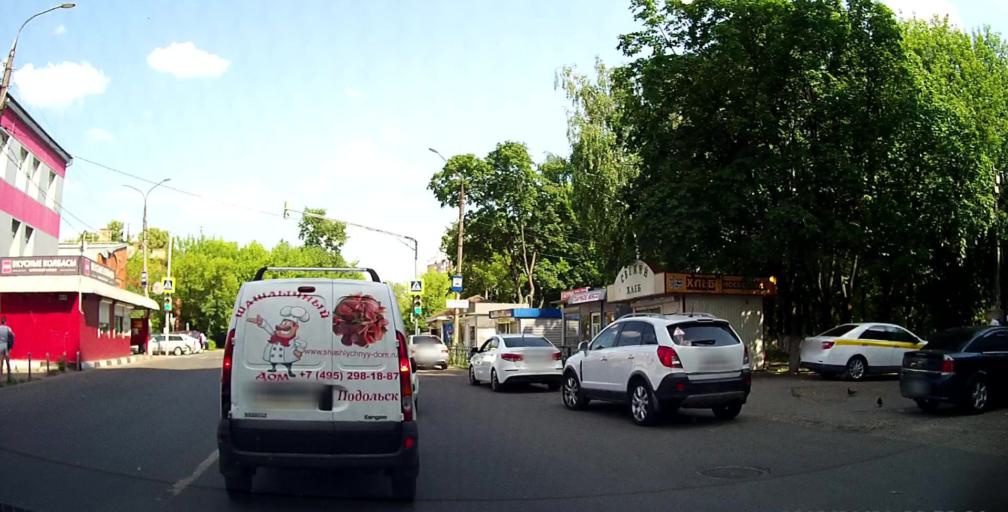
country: RU
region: Moskovskaya
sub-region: Podol'skiy Rayon
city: Podol'sk
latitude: 55.4130
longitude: 37.5386
